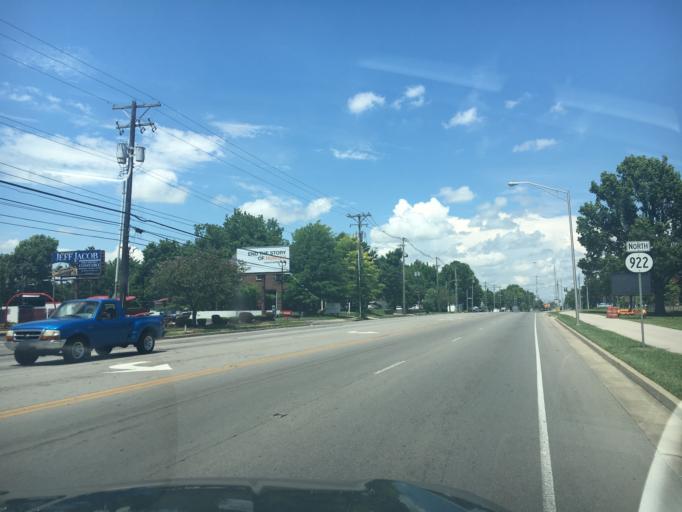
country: US
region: Kentucky
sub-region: Fayette County
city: Mount Vernon
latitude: 38.0603
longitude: -84.5008
